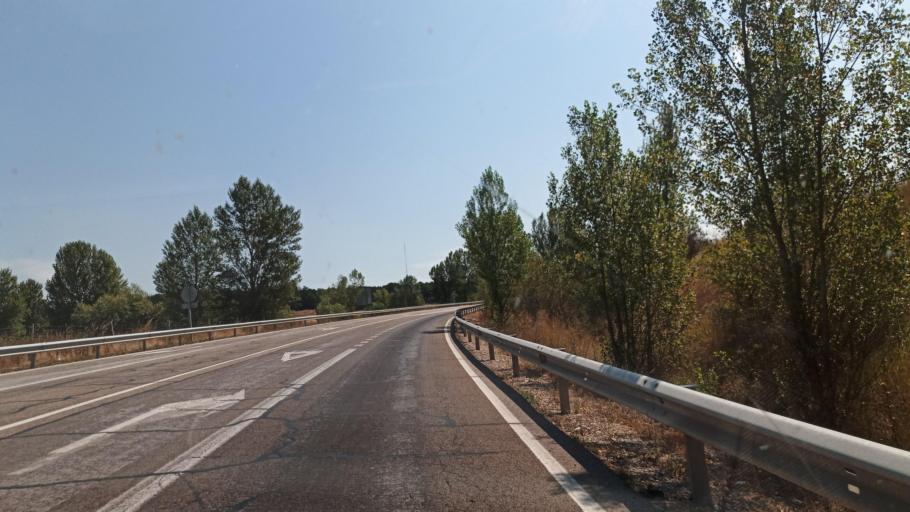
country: ES
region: Castille and Leon
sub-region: Provincia de Burgos
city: Burgos
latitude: 42.3371
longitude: -3.6789
